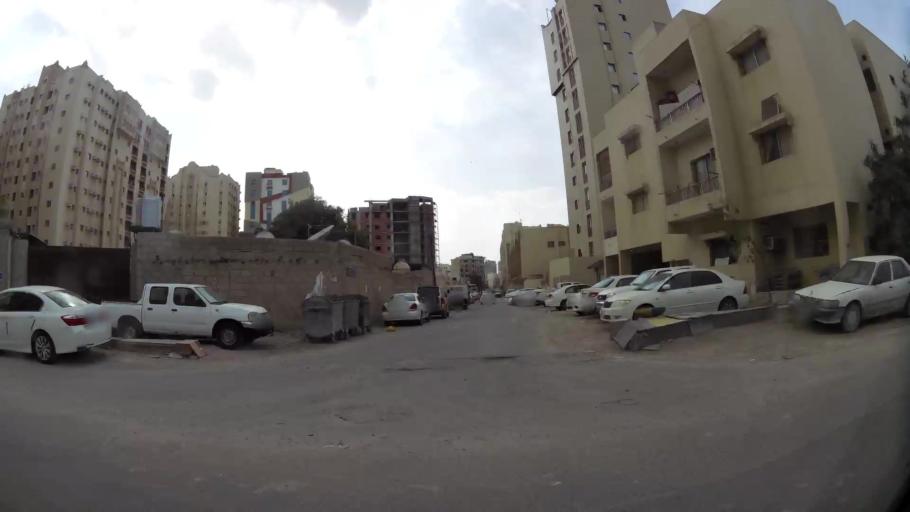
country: QA
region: Baladiyat ad Dawhah
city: Doha
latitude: 25.2828
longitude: 51.5201
